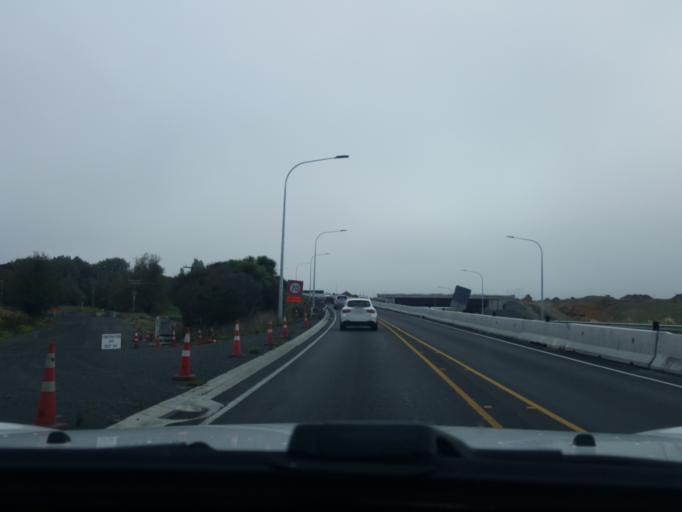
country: NZ
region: Waikato
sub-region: Waikato District
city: Te Kauwhata
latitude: -37.5120
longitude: 175.1665
